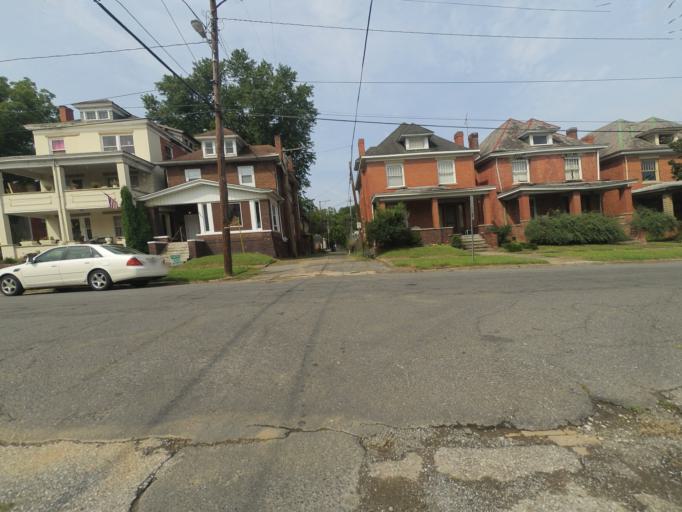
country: US
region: West Virginia
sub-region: Cabell County
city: Huntington
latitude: 38.4176
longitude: -82.4500
